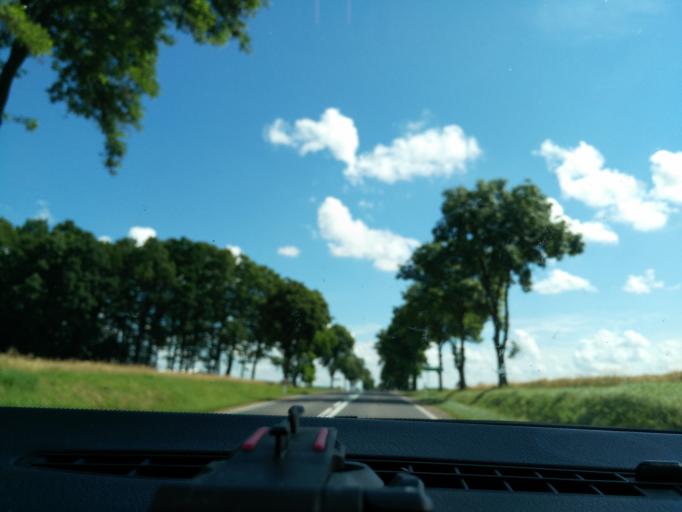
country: PL
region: Masovian Voivodeship
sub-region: Powiat losicki
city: Losice
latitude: 52.2319
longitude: 22.7603
